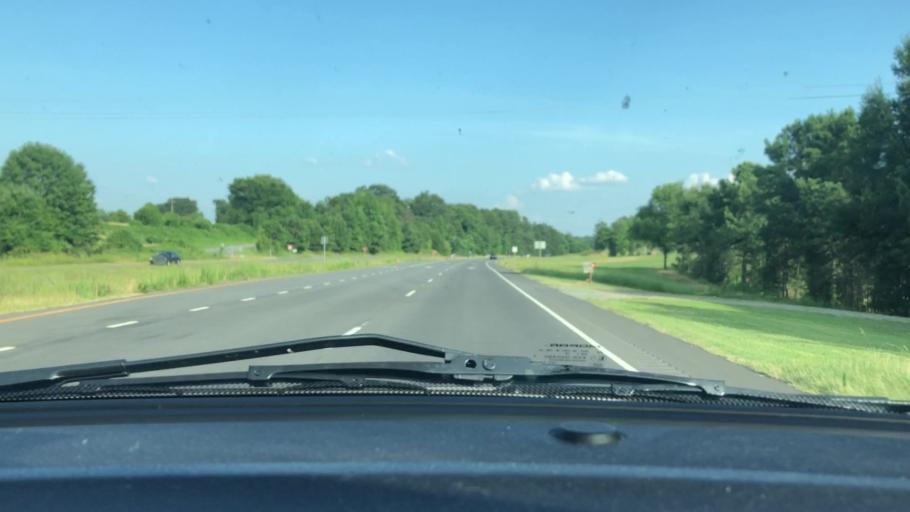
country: US
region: North Carolina
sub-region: Chatham County
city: Siler City
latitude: 35.6849
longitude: -79.4198
